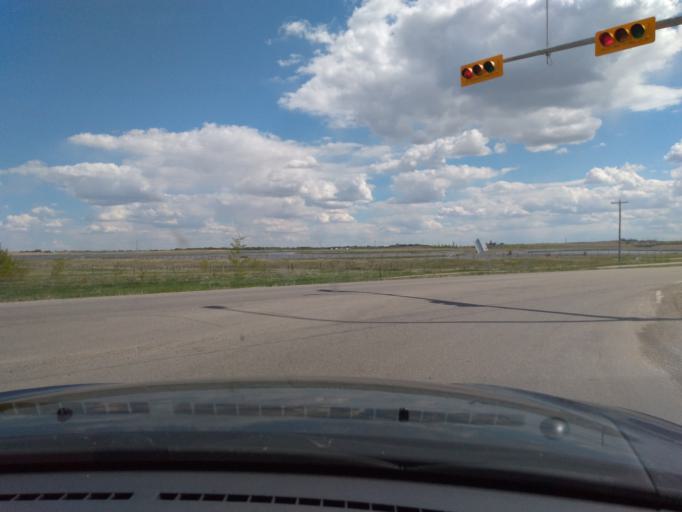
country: CA
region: Alberta
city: Chestermere
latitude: 50.9473
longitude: -113.9120
